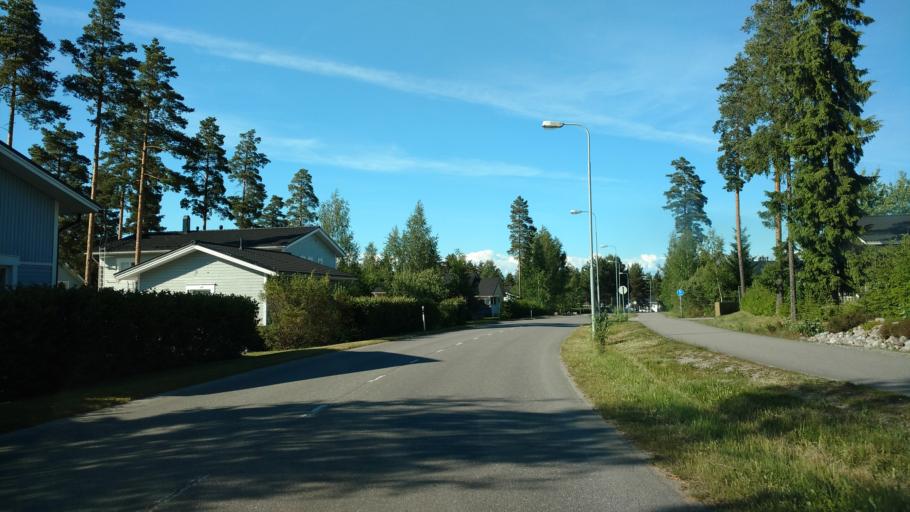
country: FI
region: Varsinais-Suomi
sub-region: Salo
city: Salo
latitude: 60.4030
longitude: 23.1883
